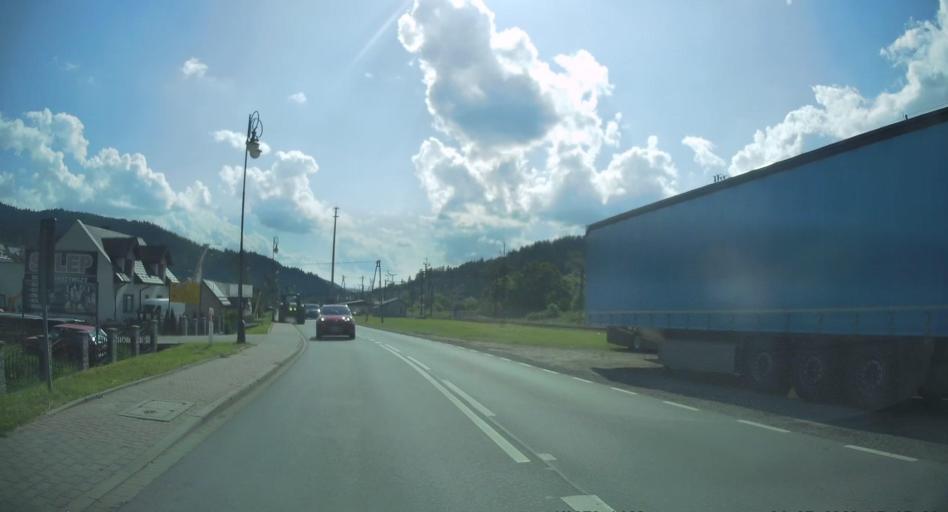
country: PL
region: Lesser Poland Voivodeship
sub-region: Powiat nowosadecki
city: Muszyna
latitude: 49.3700
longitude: 20.9445
